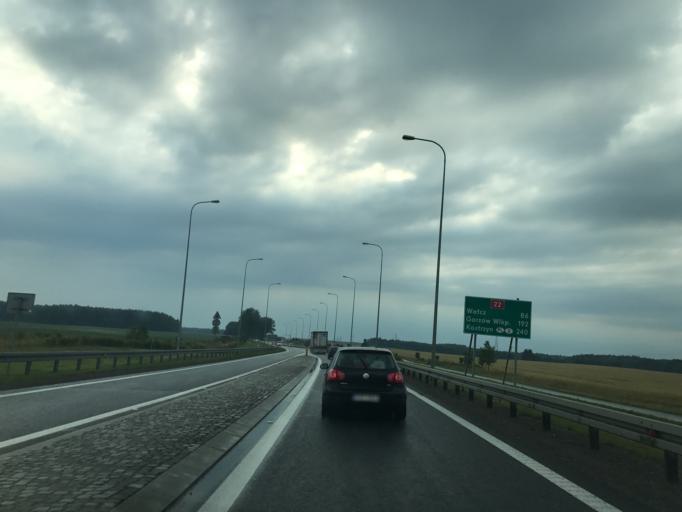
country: PL
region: Pomeranian Voivodeship
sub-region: Powiat chojnicki
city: Chojnice
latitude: 53.6888
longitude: 17.4712
